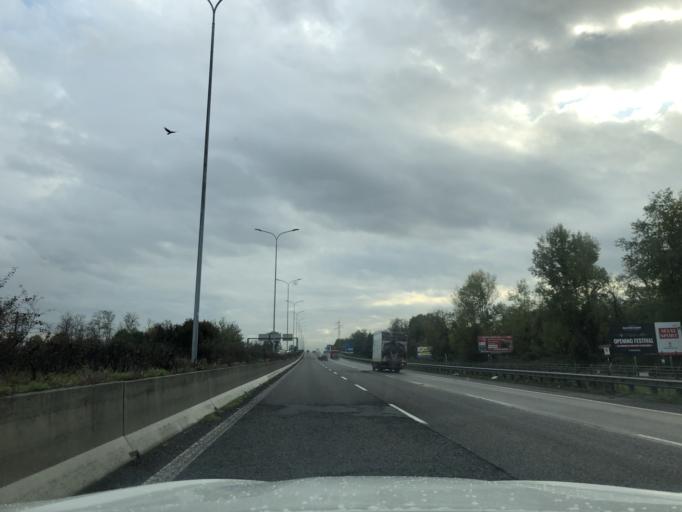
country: IT
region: Lombardy
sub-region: Provincia di Monza e Brianza
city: Santa Margherita
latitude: 45.6460
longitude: 9.2254
